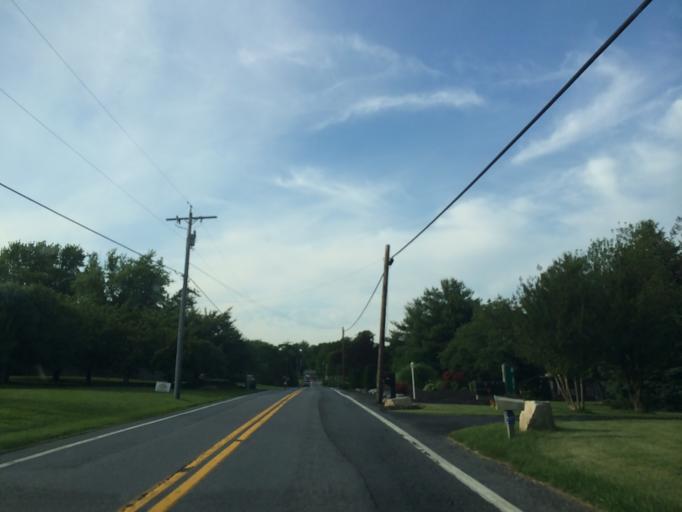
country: US
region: Maryland
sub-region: Carroll County
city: Sykesville
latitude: 39.4026
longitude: -77.0169
